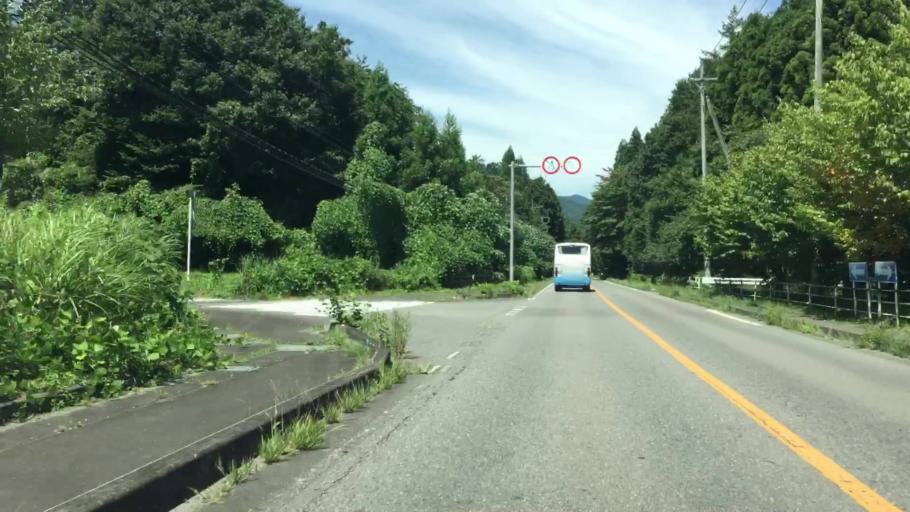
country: JP
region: Tochigi
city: Imaichi
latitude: 36.7604
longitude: 139.7270
